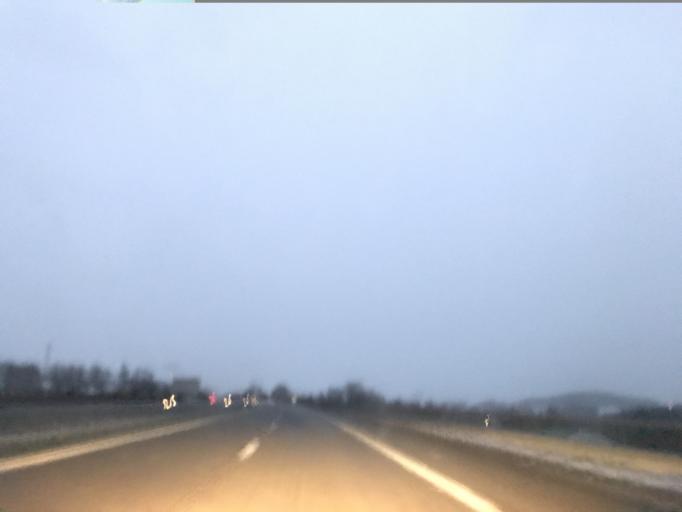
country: FR
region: Auvergne
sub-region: Departement du Puy-de-Dome
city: Saint-Ours
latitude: 45.8624
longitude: 2.8851
